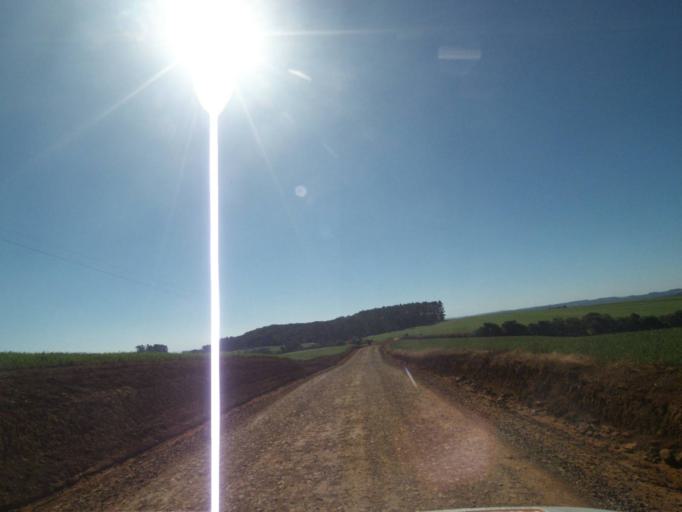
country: BR
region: Parana
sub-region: Tibagi
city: Tibagi
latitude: -24.6024
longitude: -50.6034
